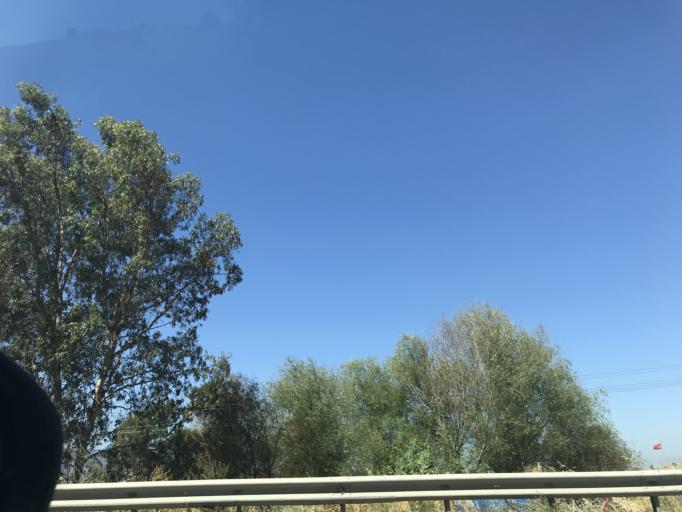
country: TR
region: Aydin
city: Cakirbeyli
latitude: 37.7664
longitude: 27.8342
